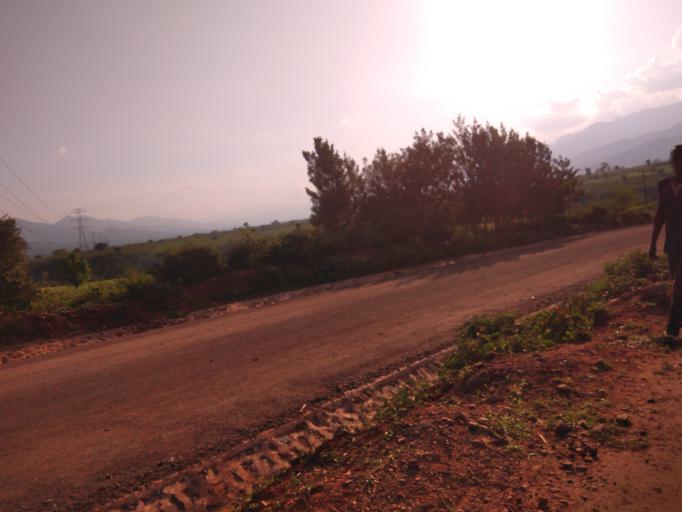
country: ET
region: Southern Nations, Nationalities, and People's Region
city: Felege Neway
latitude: 6.3926
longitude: 37.0320
